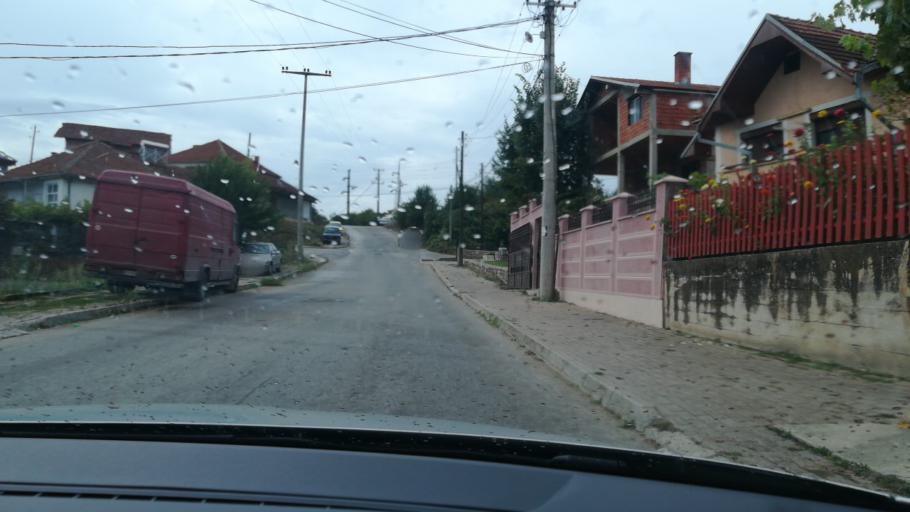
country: MK
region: Kicevo
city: Kicevo
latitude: 41.5100
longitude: 20.9481
